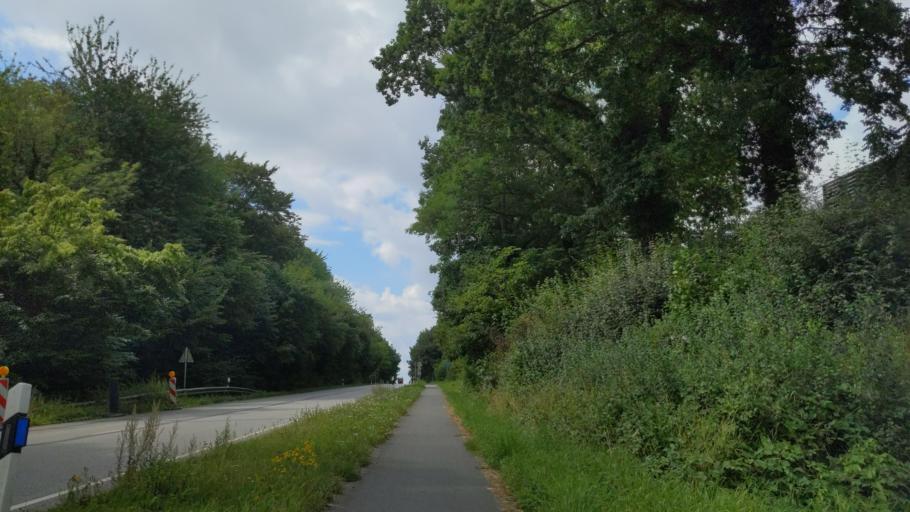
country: DE
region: Schleswig-Holstein
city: Hamberge
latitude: 53.8382
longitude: 10.5753
